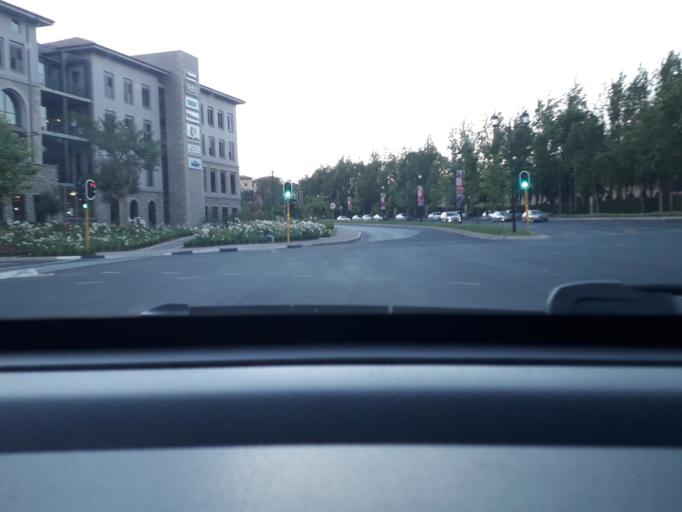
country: ZA
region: Gauteng
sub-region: City of Johannesburg Metropolitan Municipality
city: Diepsloot
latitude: -26.0265
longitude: 28.0140
